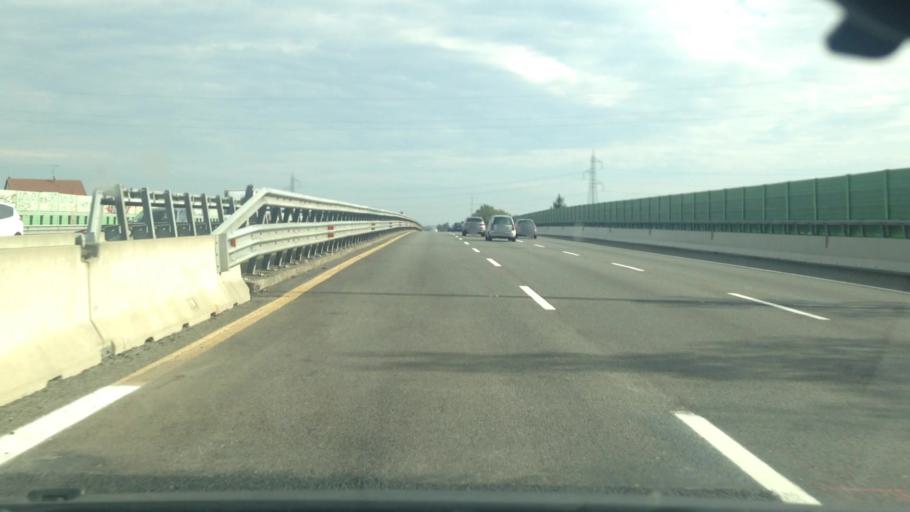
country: IT
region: Piedmont
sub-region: Provincia di Torino
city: Nichelino
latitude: 44.9883
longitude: 7.6351
